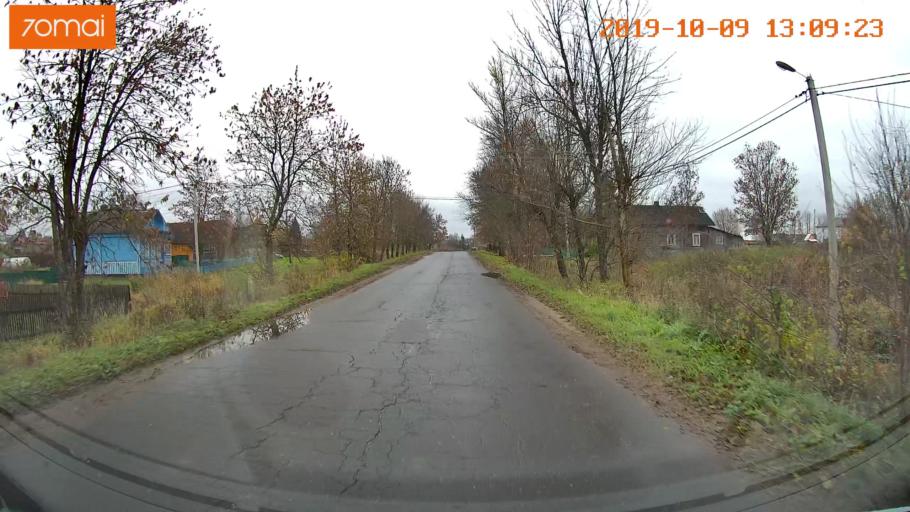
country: RU
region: Jaroslavl
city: Lyubim
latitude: 58.3562
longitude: 40.6741
